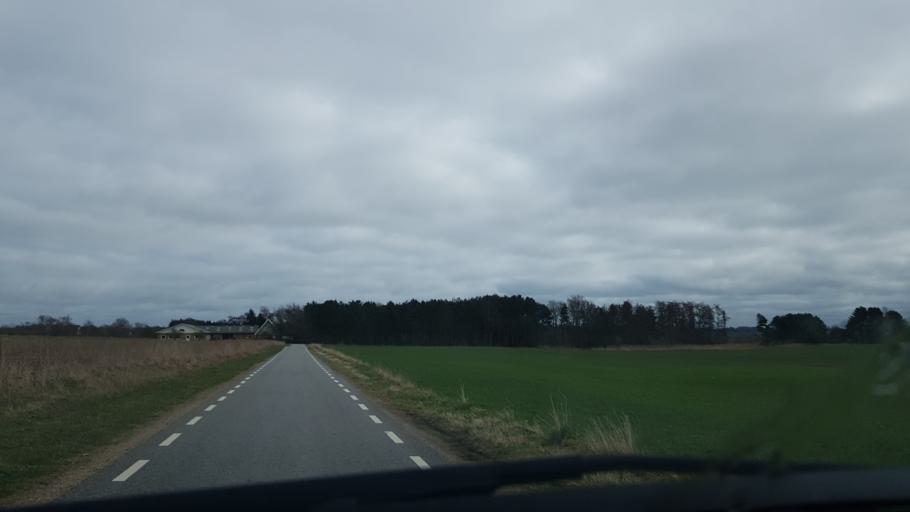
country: DK
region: Zealand
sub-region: Odsherred Kommune
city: Hojby
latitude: 55.8963
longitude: 11.5765
